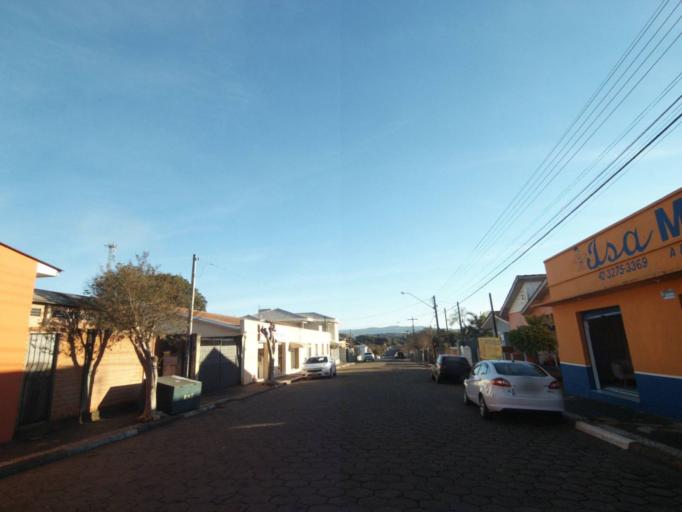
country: BR
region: Parana
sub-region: Tibagi
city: Tibagi
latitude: -24.5148
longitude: -50.4114
